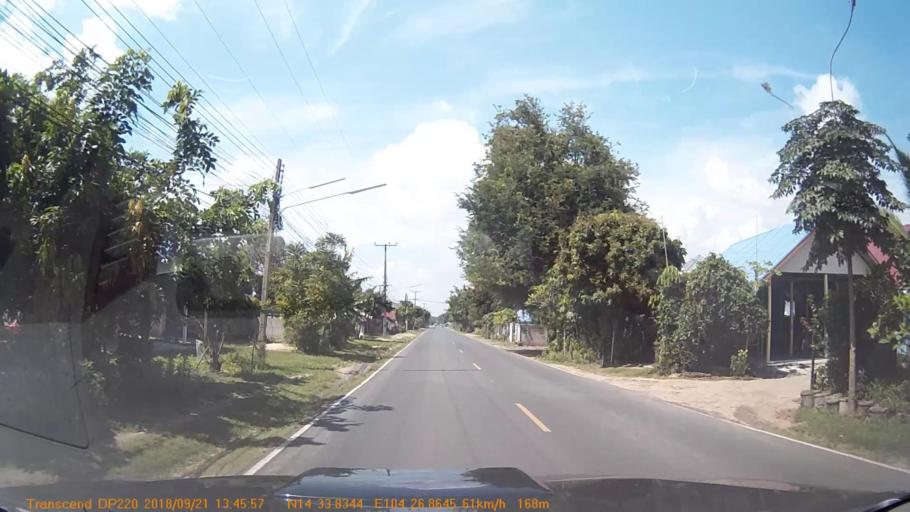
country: TH
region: Sisaket
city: Khun Han
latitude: 14.5642
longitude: 104.4477
